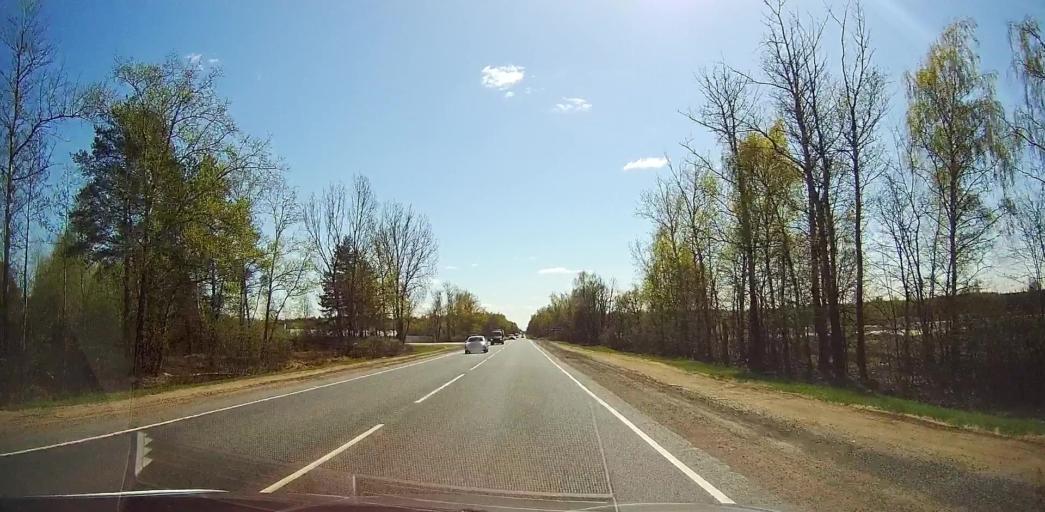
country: RU
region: Moskovskaya
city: Gzhel'
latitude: 55.5730
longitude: 38.3910
